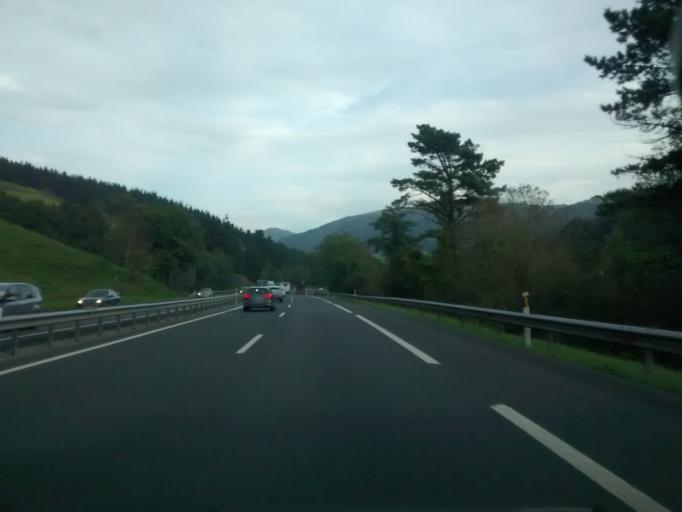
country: ES
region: Basque Country
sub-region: Provincia de Guipuzcoa
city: Cestona
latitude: 43.2660
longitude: -2.2991
